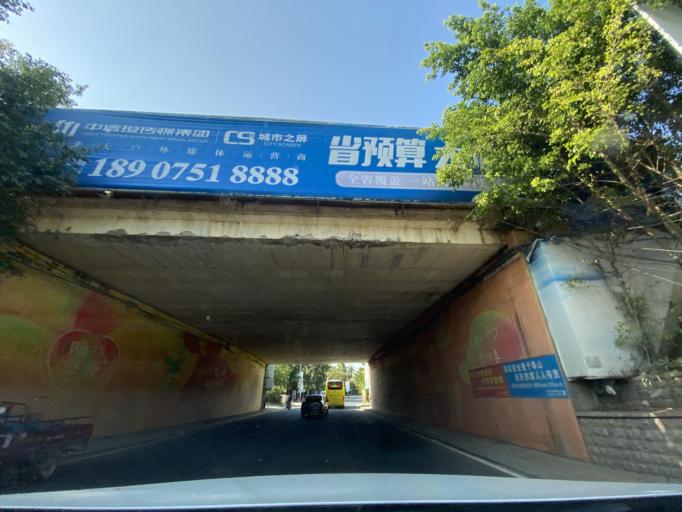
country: CN
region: Hainan
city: Yingzhou
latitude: 18.4370
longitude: 109.8500
